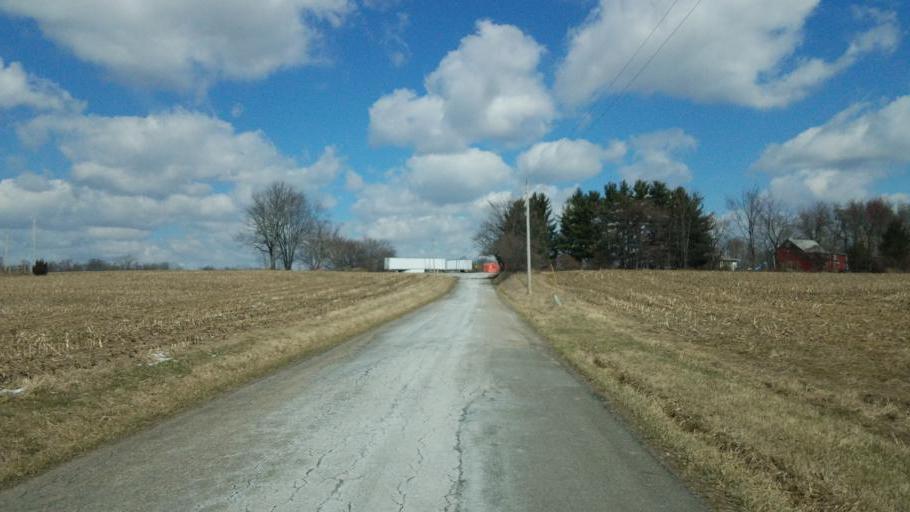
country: US
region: Ohio
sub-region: Knox County
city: Mount Vernon
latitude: 40.3301
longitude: -82.5698
